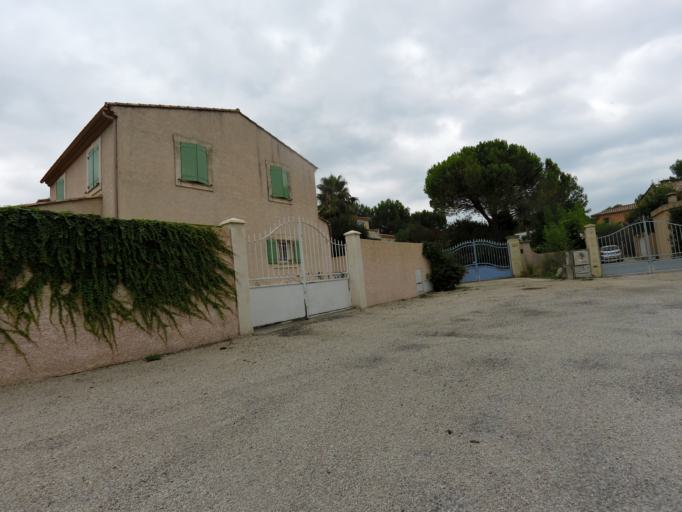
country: FR
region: Languedoc-Roussillon
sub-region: Departement de l'Herault
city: Villetelle
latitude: 43.7275
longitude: 4.1347
